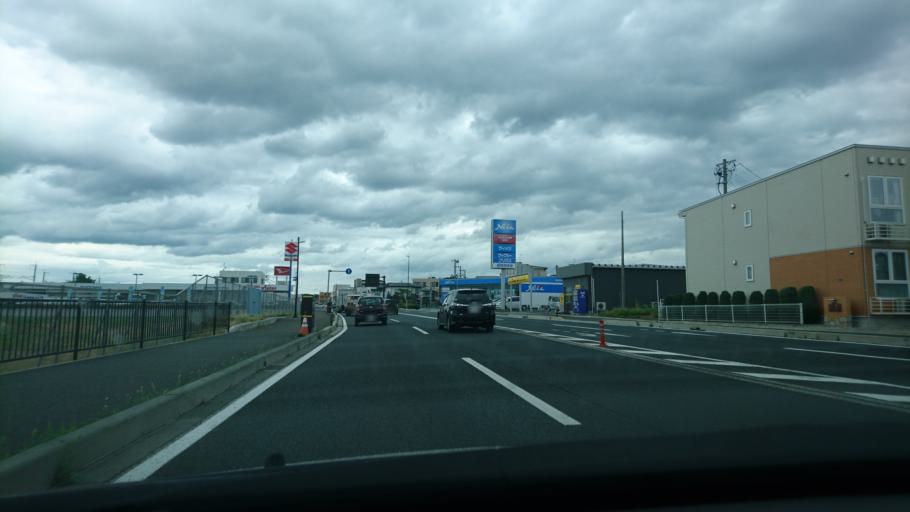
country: JP
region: Iwate
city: Morioka-shi
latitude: 39.7395
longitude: 141.1272
